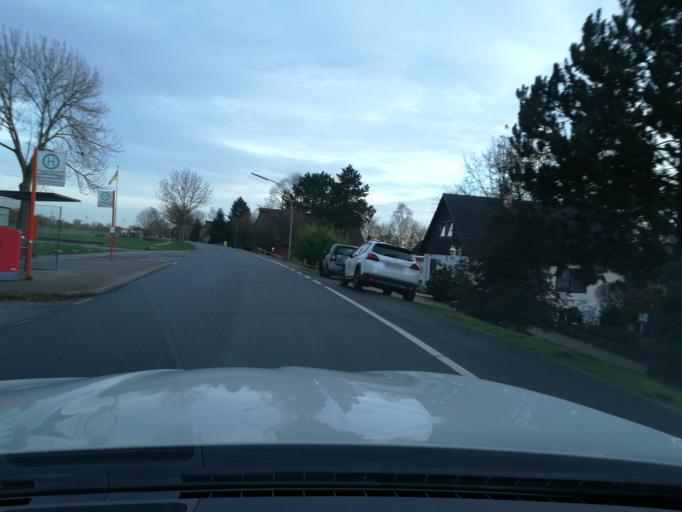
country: DE
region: Hamburg
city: Harburg
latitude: 53.4679
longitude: 10.0363
